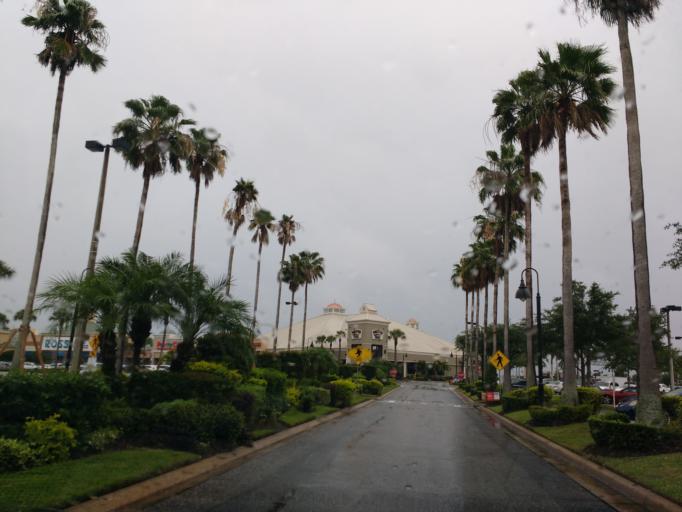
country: US
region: Florida
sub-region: Sarasota County
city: The Meadows
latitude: 27.3907
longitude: -82.4538
